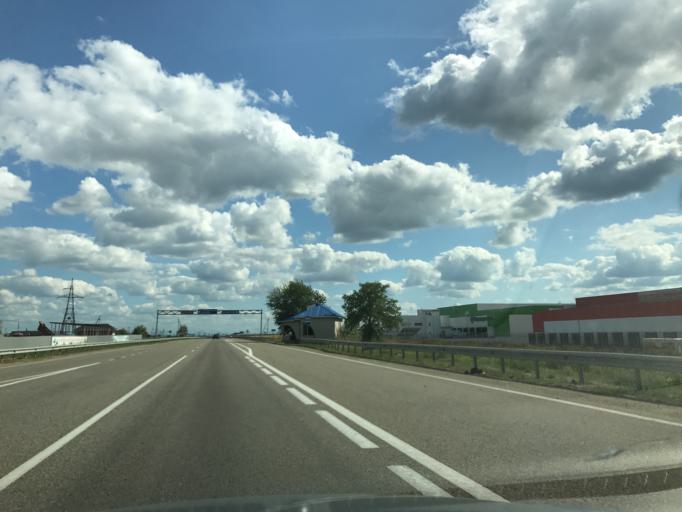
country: RU
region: Adygeya
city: Adygeysk
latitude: 44.8751
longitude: 39.1820
